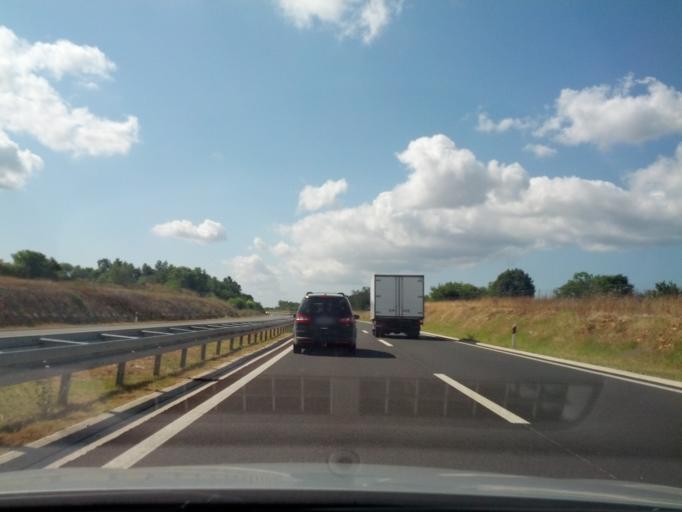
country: HR
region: Istarska
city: Vodnjan
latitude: 45.0019
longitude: 13.8374
